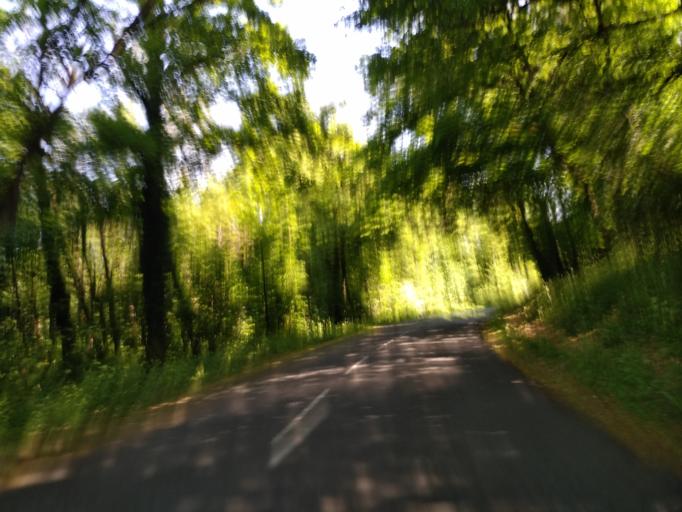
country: FR
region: Rhone-Alpes
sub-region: Departement du Rhone
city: Limonest
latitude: 45.8318
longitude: 4.8015
